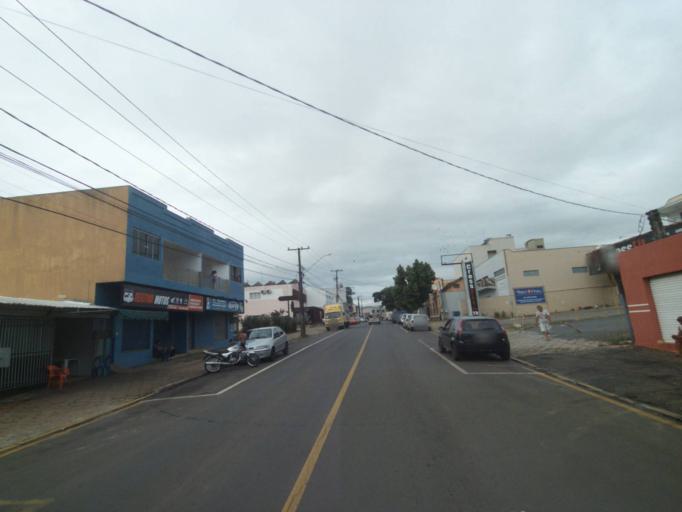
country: BR
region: Parana
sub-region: Telemaco Borba
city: Telemaco Borba
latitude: -24.3300
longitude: -50.6315
